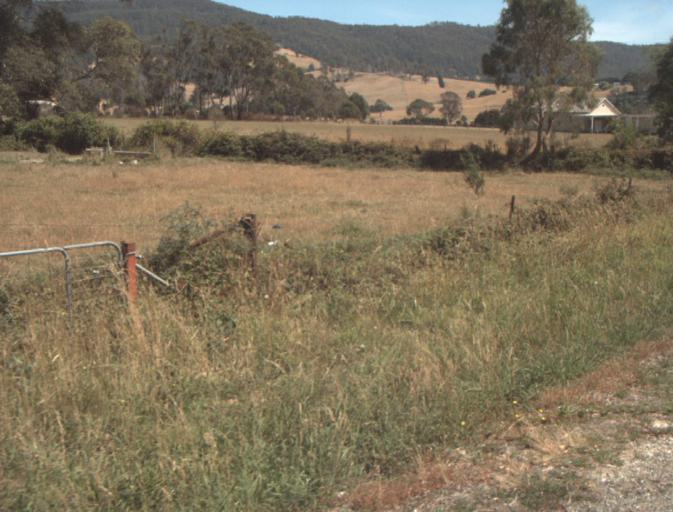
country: AU
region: Tasmania
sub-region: Launceston
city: Mayfield
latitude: -41.2549
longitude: 147.1500
